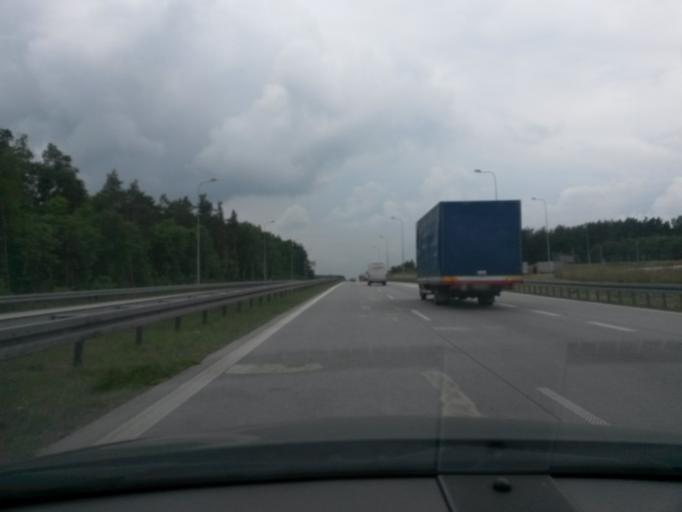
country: PL
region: Lodz Voivodeship
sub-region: Powiat rawski
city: Rawa Mazowiecka
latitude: 51.8207
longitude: 20.3187
